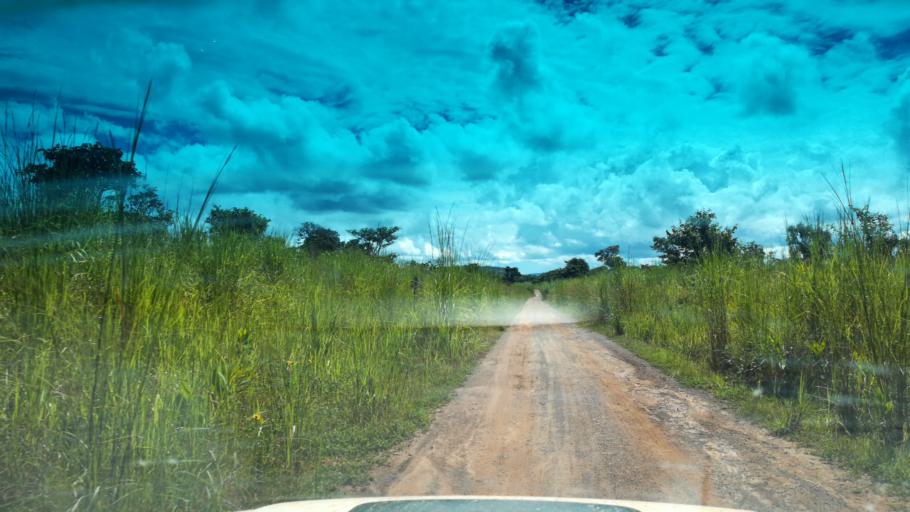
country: ZM
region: Northern
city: Kaputa
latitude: -7.7866
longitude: 29.2152
